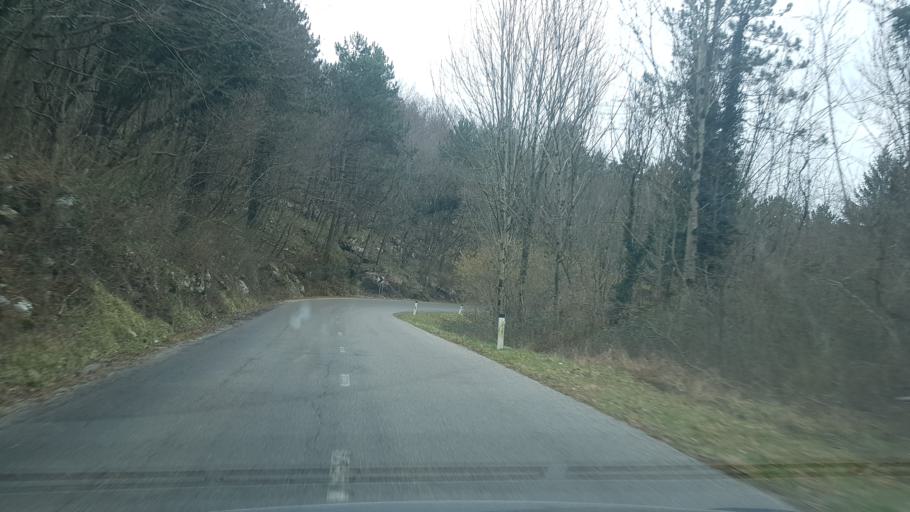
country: SI
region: Kanal
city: Deskle
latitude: 46.0370
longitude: 13.6719
